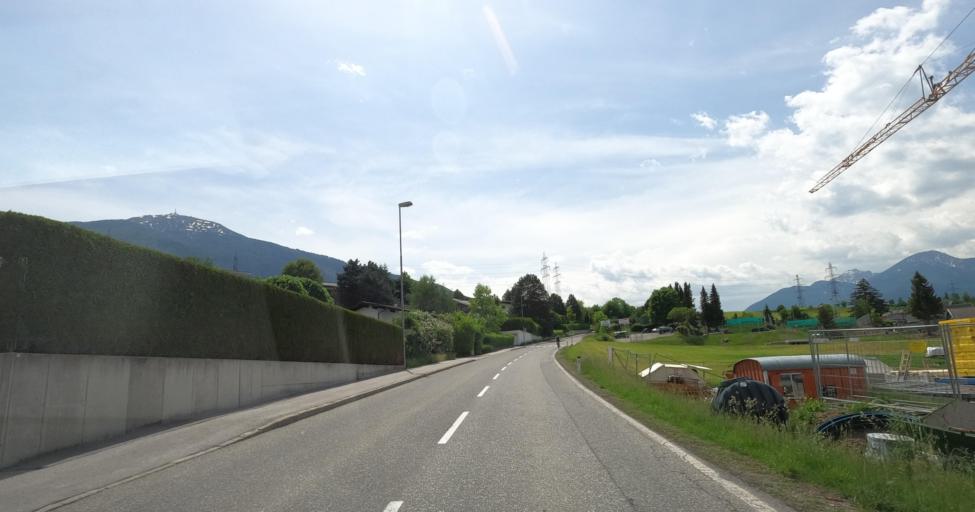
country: AT
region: Tyrol
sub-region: Politischer Bezirk Innsbruck Land
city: Aldrans
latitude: 47.2455
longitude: 11.4391
